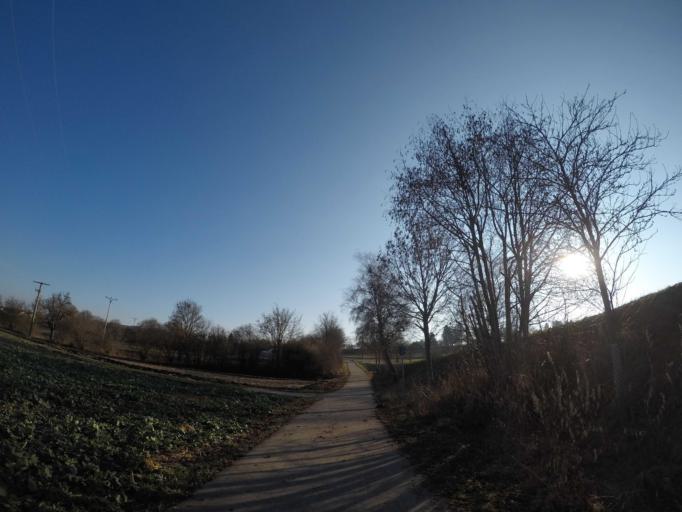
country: DE
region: Baden-Wuerttemberg
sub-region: Tuebingen Region
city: Langenau
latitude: 48.4745
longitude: 10.0747
